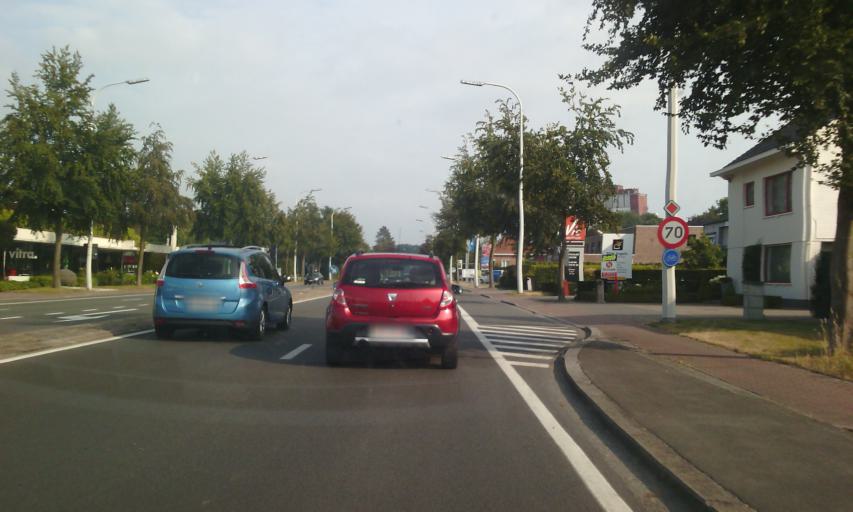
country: BE
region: Flanders
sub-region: Provincie Oost-Vlaanderen
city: Lovendegem
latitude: 51.0966
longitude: 3.6395
